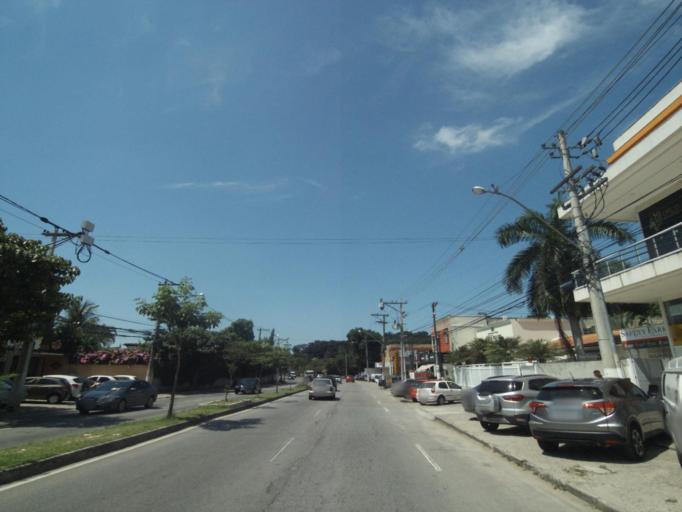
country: BR
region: Rio de Janeiro
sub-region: Niteroi
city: Niteroi
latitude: -22.9065
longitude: -43.0558
